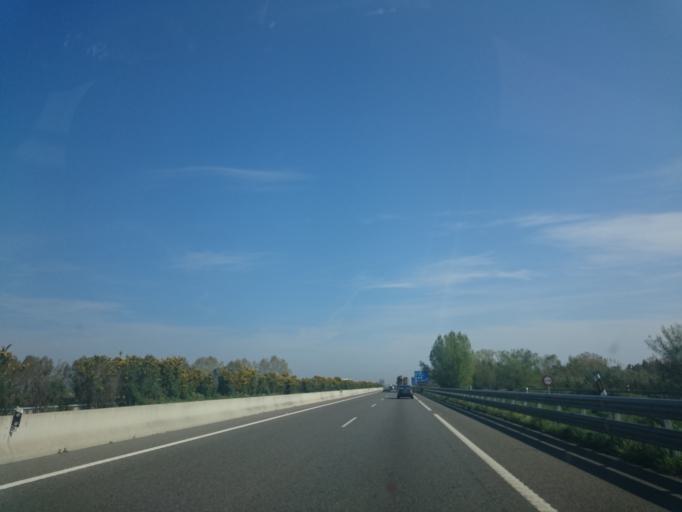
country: ES
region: Catalonia
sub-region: Provincia de Girona
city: Riudellots de la Selva
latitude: 41.8762
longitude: 2.7796
